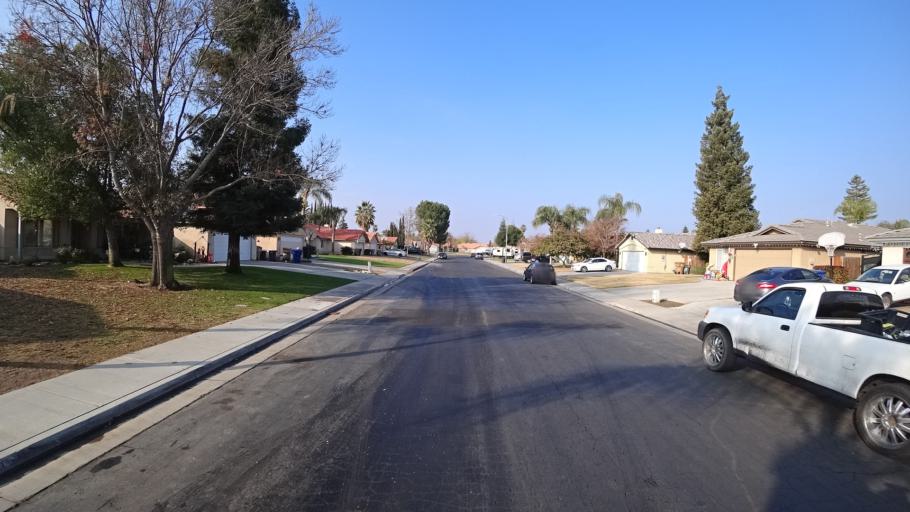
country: US
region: California
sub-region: Kern County
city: Greenfield
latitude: 35.3046
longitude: -119.0679
